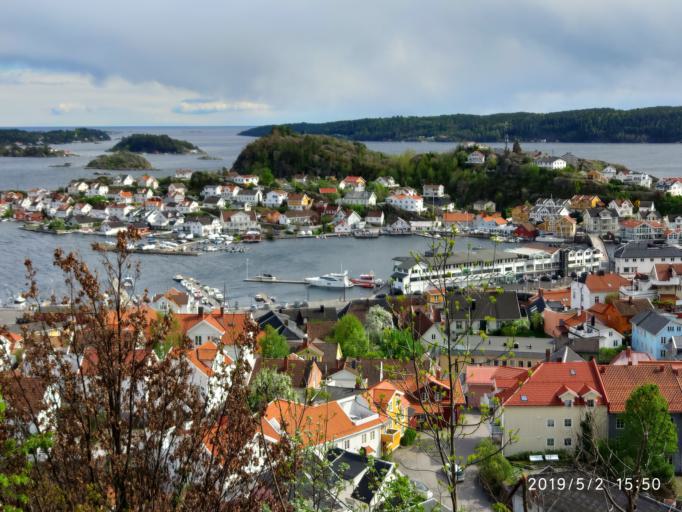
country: NO
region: Telemark
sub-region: Kragero
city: Kragero
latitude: 58.8711
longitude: 9.4115
